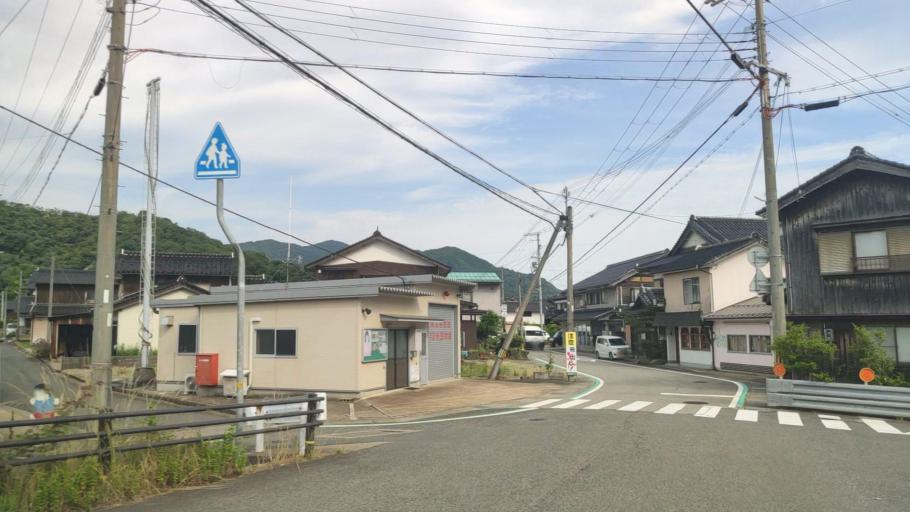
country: JP
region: Hyogo
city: Toyooka
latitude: 35.6385
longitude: 134.8392
